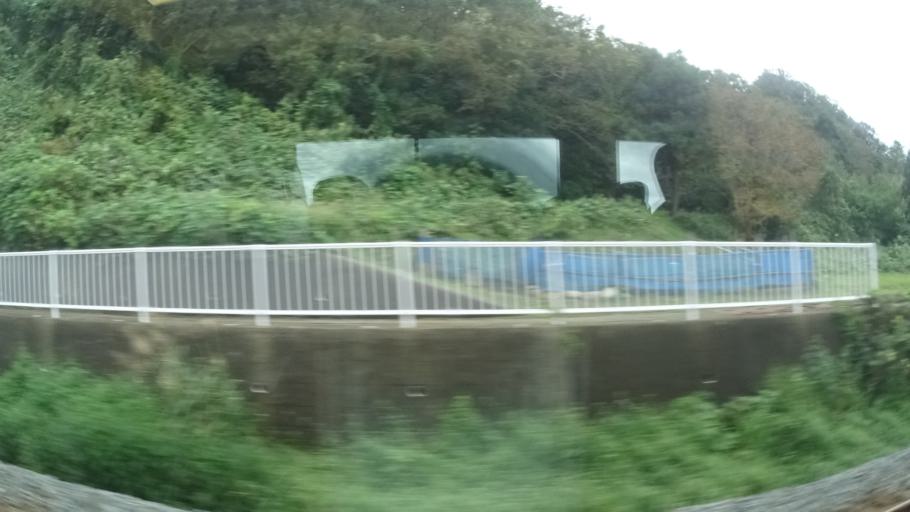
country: JP
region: Niigata
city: Murakami
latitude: 38.3227
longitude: 139.4516
